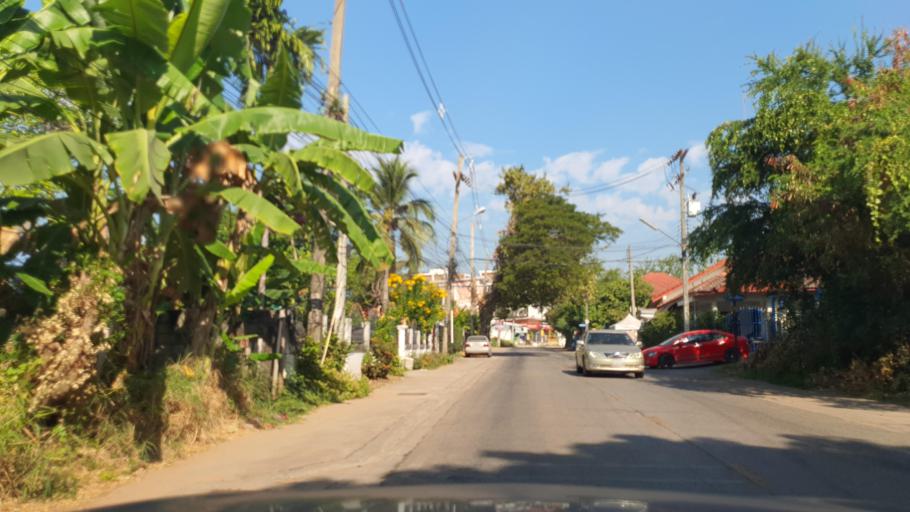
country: TH
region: Khon Kaen
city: Khon Kaen
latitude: 16.4380
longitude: 102.8138
